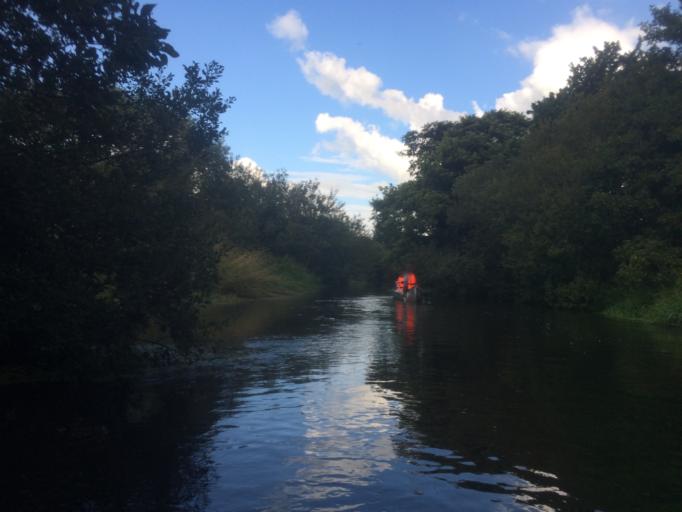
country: DK
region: South Denmark
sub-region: Vejle Kommune
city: Egtved
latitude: 55.6658
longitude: 9.3353
